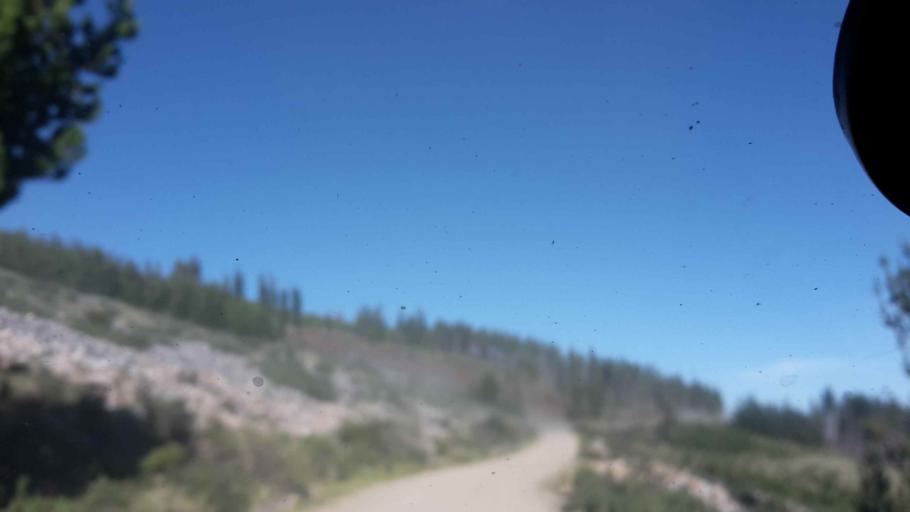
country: BO
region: Cochabamba
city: Arani
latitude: -17.7120
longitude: -65.6828
